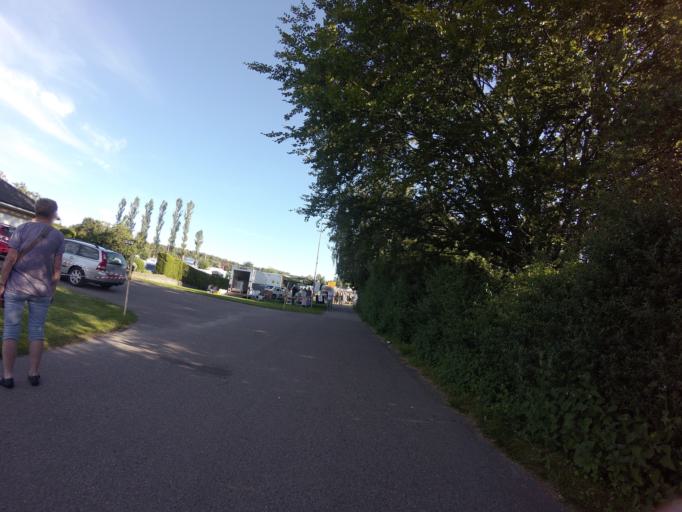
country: SE
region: Skane
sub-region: Sjobo Kommun
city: Sjoebo
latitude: 55.6317
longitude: 13.7111
